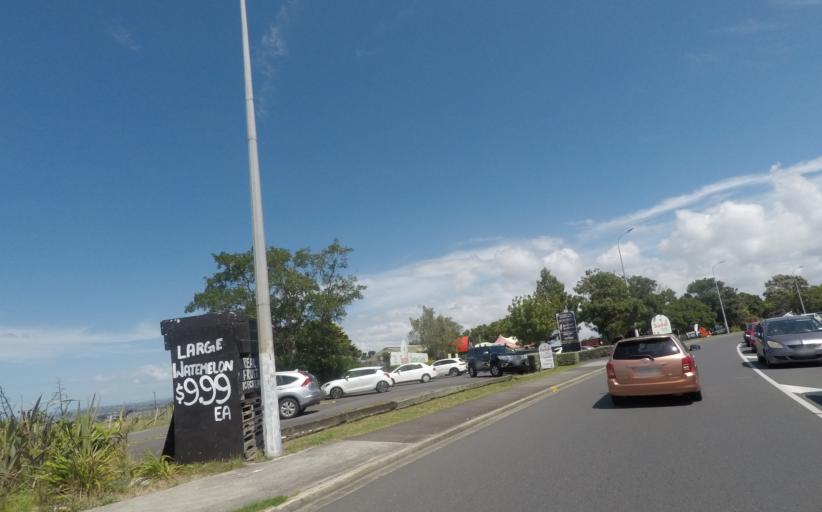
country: NZ
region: Auckland
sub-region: Auckland
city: Tamaki
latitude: -36.8696
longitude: 174.8457
